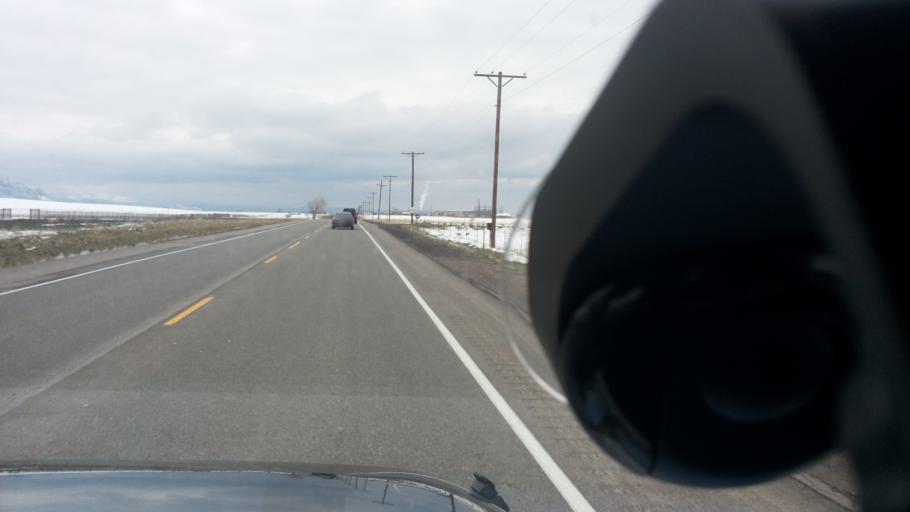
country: US
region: Colorado
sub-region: Boulder County
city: Superior
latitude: 39.8763
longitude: -105.2411
